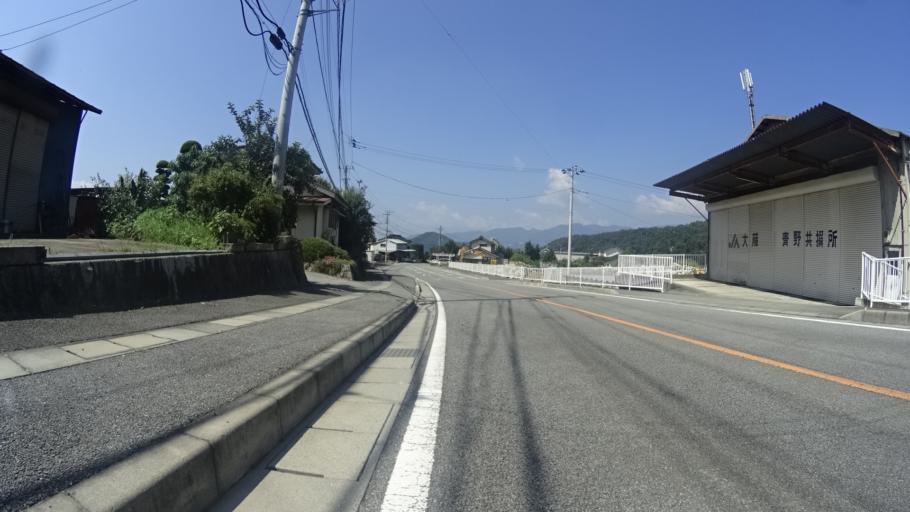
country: JP
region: Yamanashi
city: Enzan
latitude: 35.7216
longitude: 138.7508
